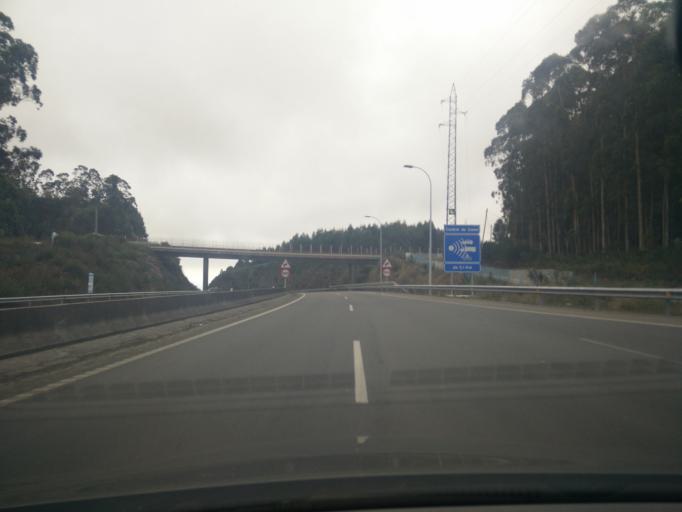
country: ES
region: Galicia
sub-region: Provincia da Coruna
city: Arteixo
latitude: 43.2766
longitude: -8.5272
